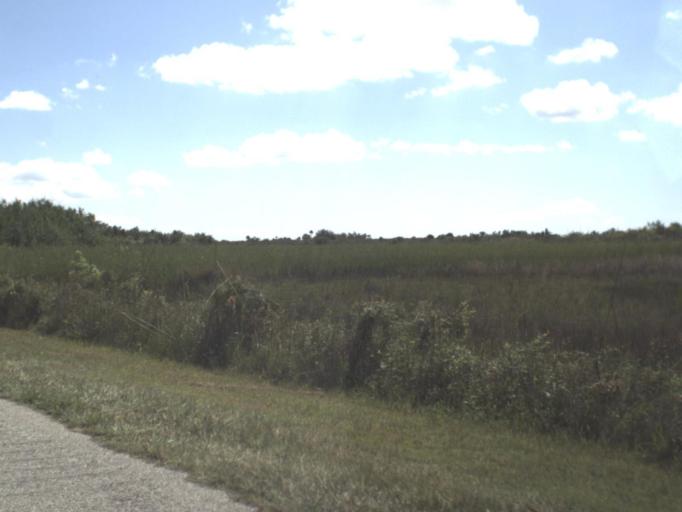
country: US
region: Florida
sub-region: Collier County
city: Marco
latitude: 25.9531
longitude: -81.4853
